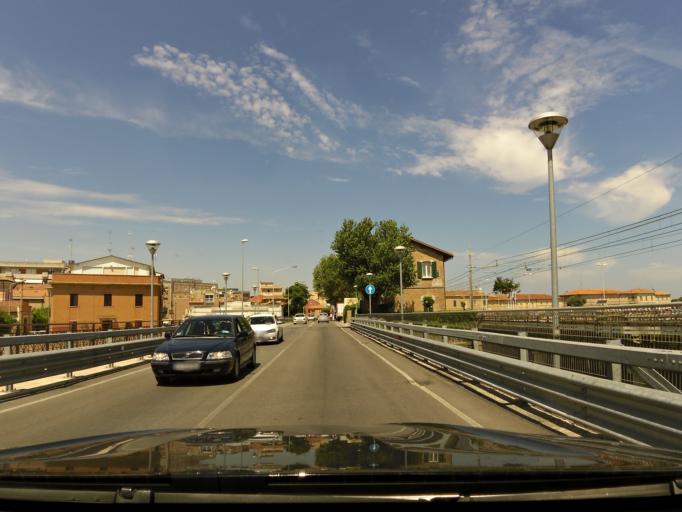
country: IT
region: The Marches
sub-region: Provincia di Ancona
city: Senigallia
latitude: 43.7172
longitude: 13.2199
